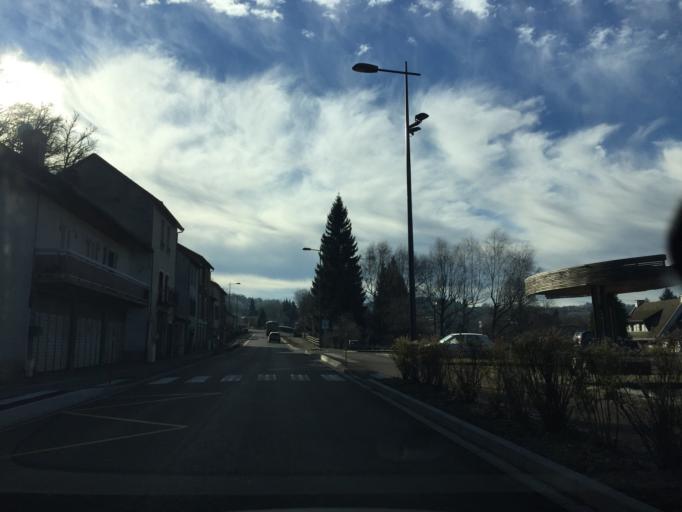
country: FR
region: Auvergne
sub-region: Departement du Puy-de-Dome
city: Gelles
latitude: 45.8661
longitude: 2.6747
